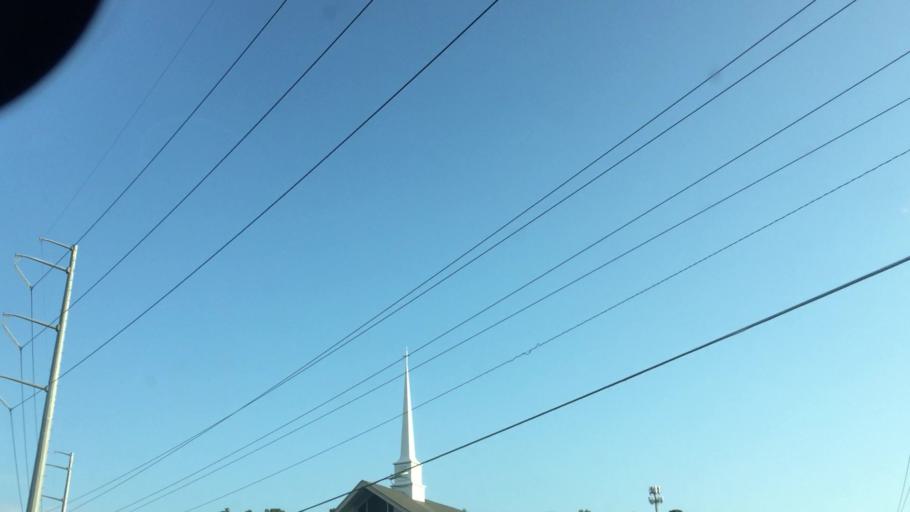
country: US
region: Georgia
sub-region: DeKalb County
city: Panthersville
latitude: 33.7046
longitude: -84.2146
